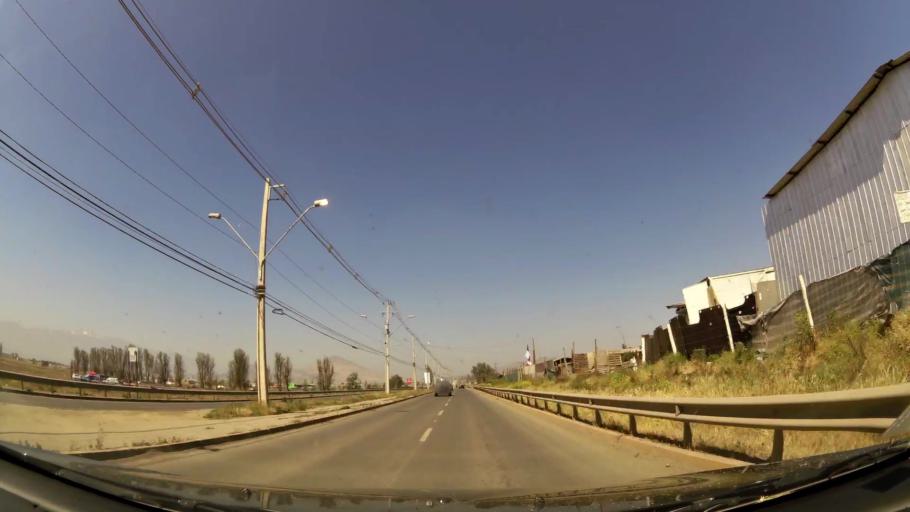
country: CL
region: Santiago Metropolitan
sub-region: Provincia de Santiago
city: Lo Prado
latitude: -33.3449
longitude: -70.7413
